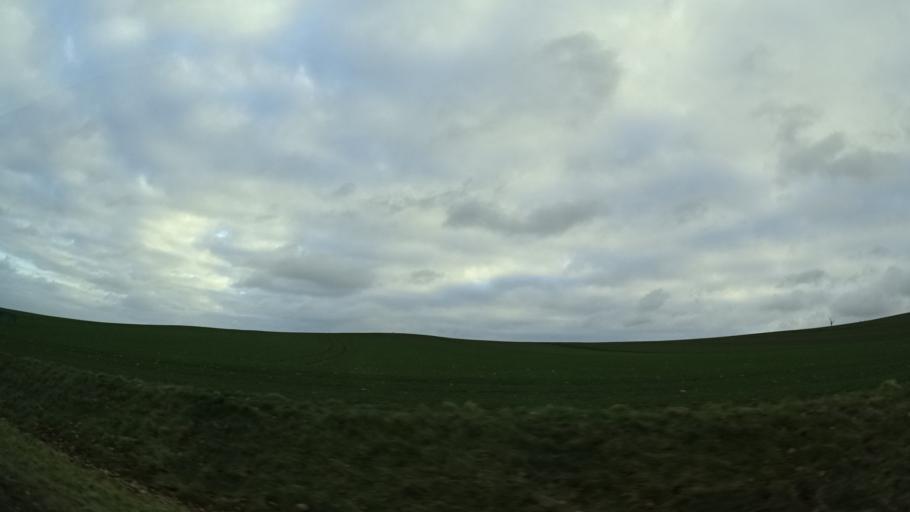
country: DE
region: Thuringia
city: Dreitzsch
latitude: 50.7258
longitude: 11.8008
